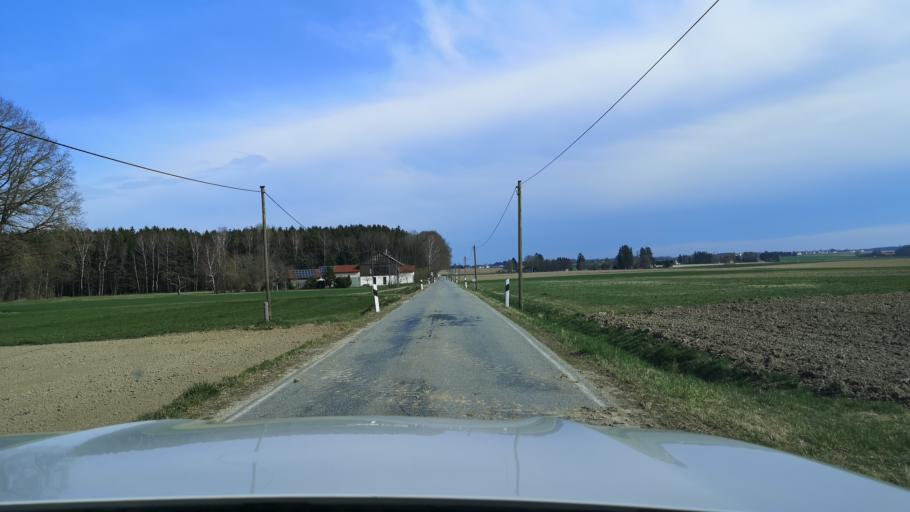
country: DE
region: Bavaria
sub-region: Upper Bavaria
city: Pastetten
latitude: 48.2155
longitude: 11.9653
